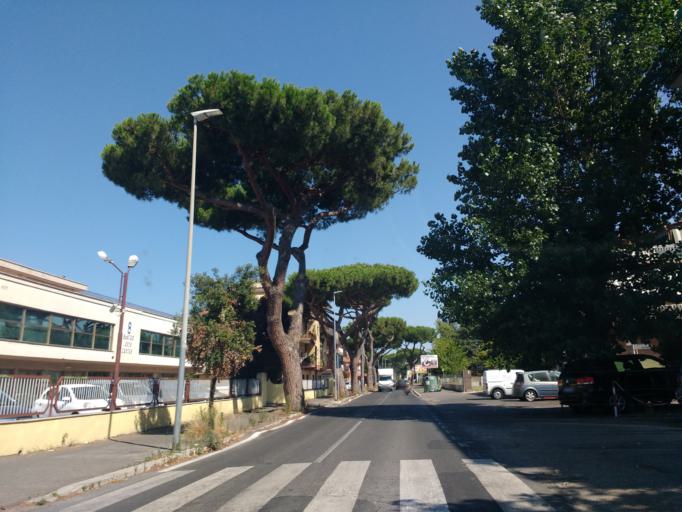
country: IT
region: Latium
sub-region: Citta metropolitana di Roma Capitale
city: Acilia-Castel Fusano-Ostia Antica
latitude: 41.7771
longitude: 12.3690
